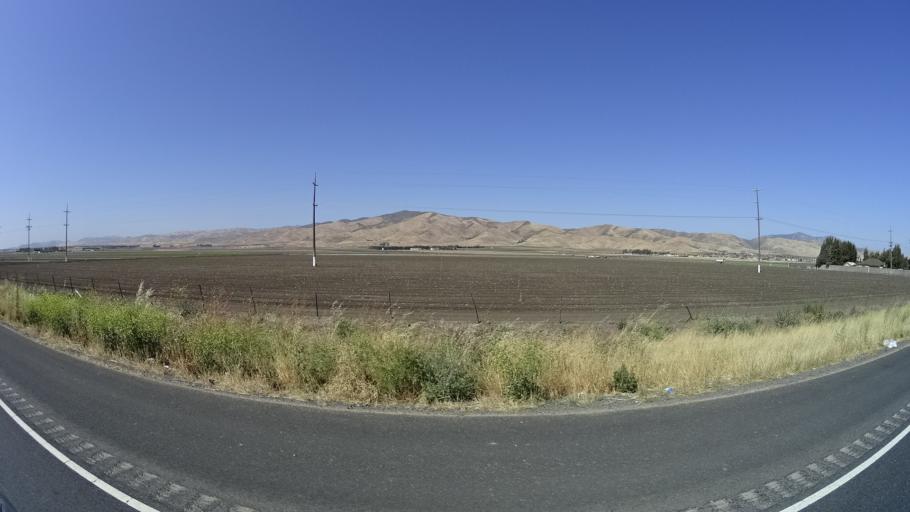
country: US
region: California
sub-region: Monterey County
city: Soledad
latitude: 36.4392
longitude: -121.3485
